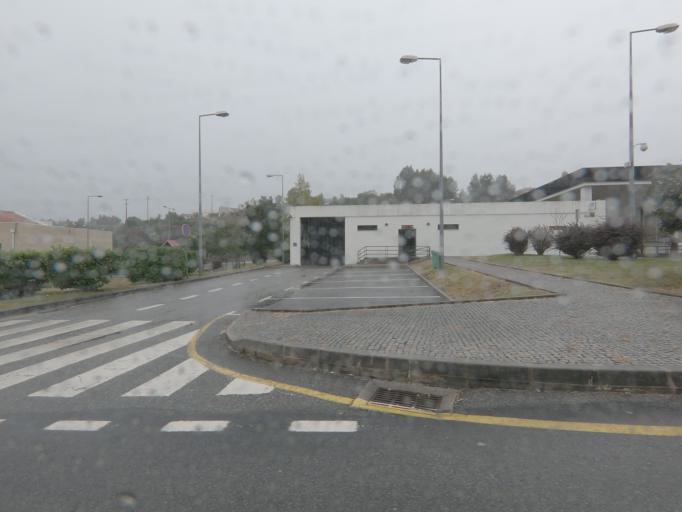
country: PT
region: Porto
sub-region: Marco de Canaveses
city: Marco de Canavezes
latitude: 41.2331
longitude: -8.1785
